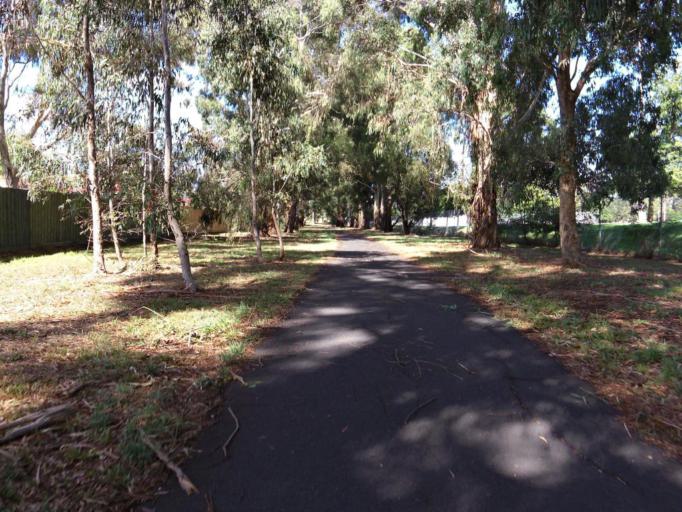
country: AU
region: Victoria
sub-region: Knox
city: Knoxfield
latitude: -37.8963
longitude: 145.2595
